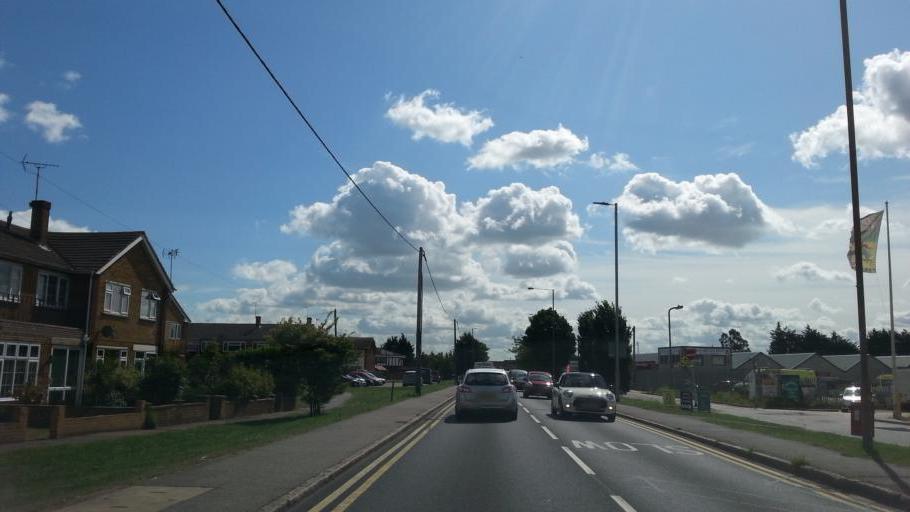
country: GB
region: England
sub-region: Essex
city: Canvey Island
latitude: 51.5219
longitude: 0.5598
